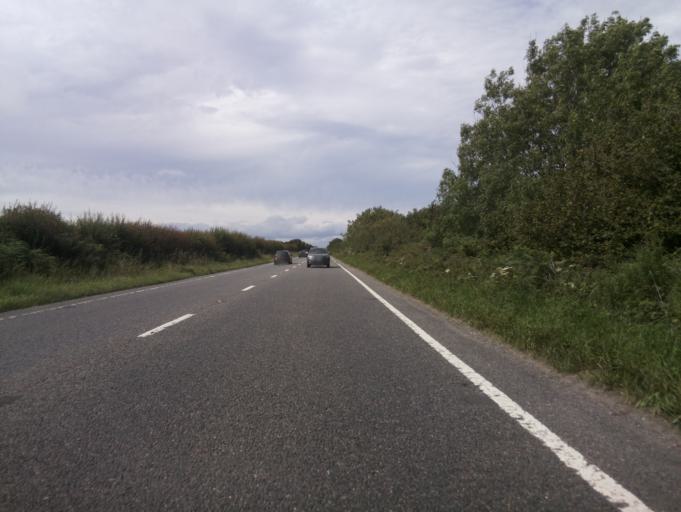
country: GB
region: England
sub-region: Dorset
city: Sherborne
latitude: 50.8100
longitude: -2.5537
